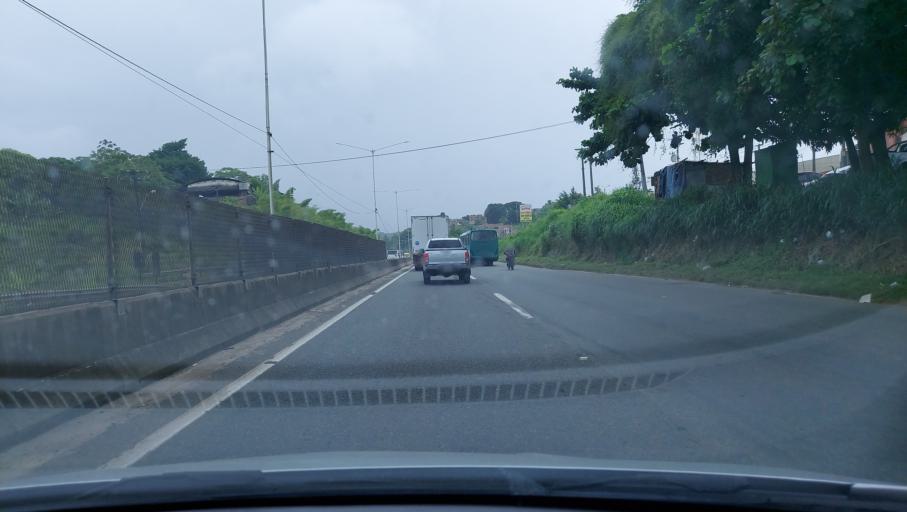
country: BR
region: Bahia
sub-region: Simoes Filho
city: Simoes Filho
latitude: -12.8867
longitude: -38.4390
